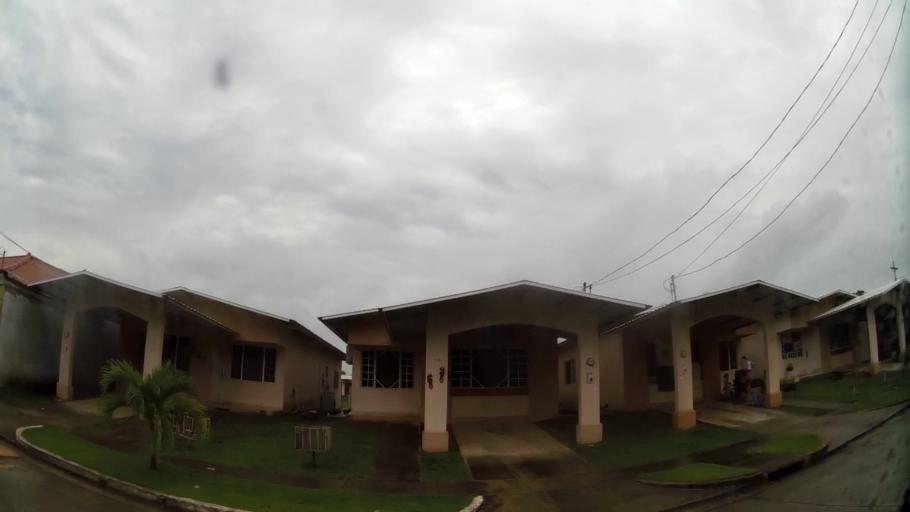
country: PA
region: Colon
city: Arco Iris
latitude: 9.3314
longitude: -79.8837
